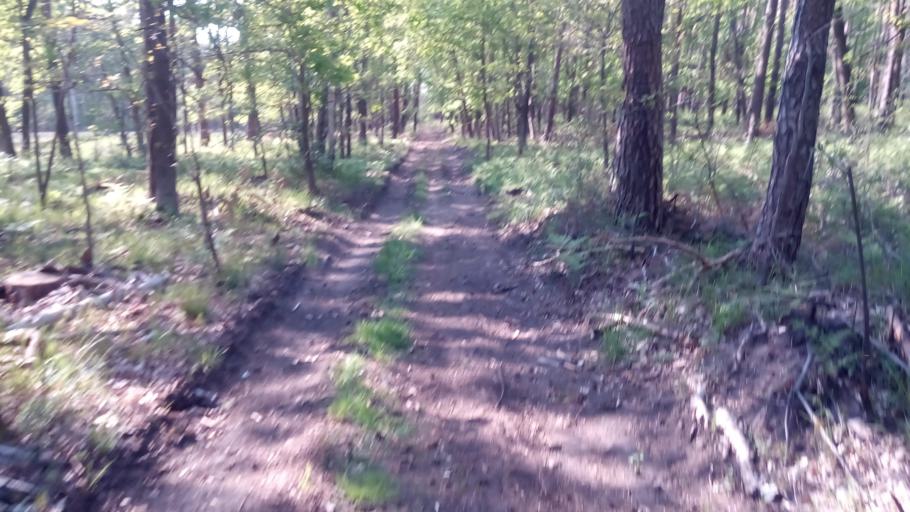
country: PL
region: Opole Voivodeship
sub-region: Powiat opolski
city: Tarnow Opolski
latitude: 50.5856
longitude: 18.0527
